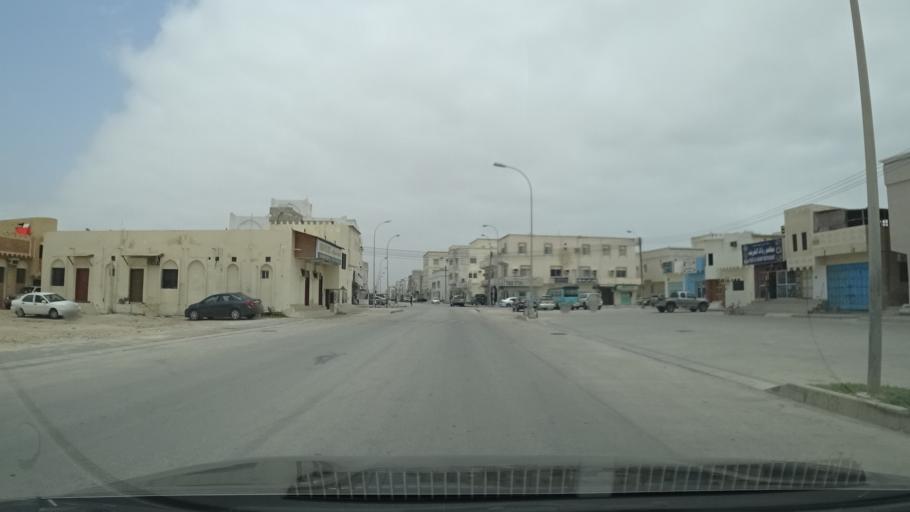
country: OM
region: Zufar
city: Salalah
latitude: 17.0221
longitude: 54.1583
